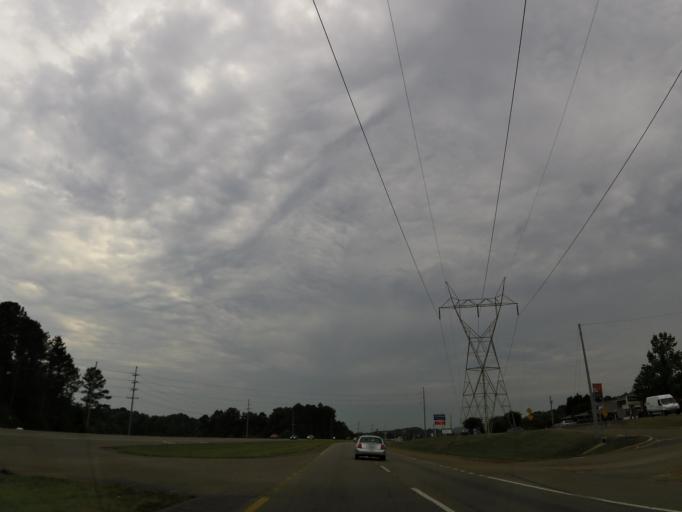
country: US
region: Alabama
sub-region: Jackson County
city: Scottsboro
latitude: 34.6542
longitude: -86.0239
